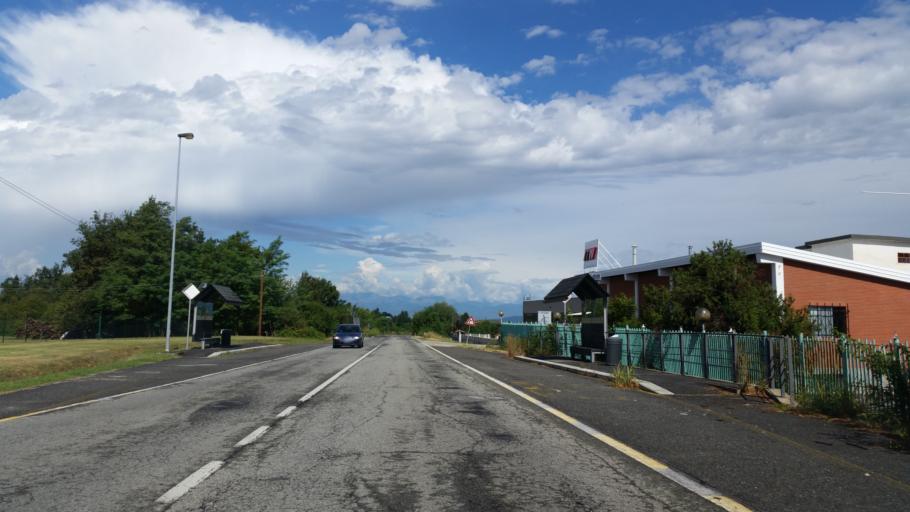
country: IT
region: Piedmont
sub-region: Provincia di Torino
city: Pralormo
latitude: 44.8734
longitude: 7.8900
